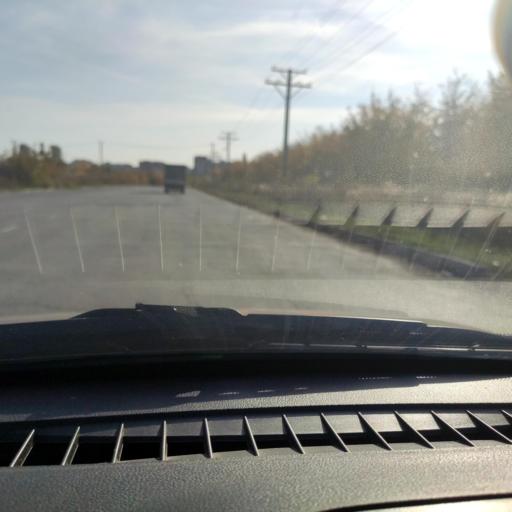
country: RU
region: Samara
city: Tol'yatti
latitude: 53.5560
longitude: 49.3290
